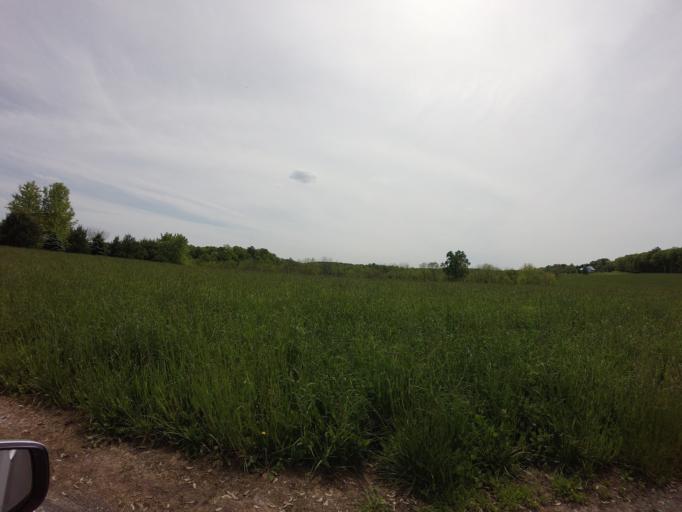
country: US
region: Maryland
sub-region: Carroll County
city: Eldersburg
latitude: 39.4758
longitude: -77.0157
